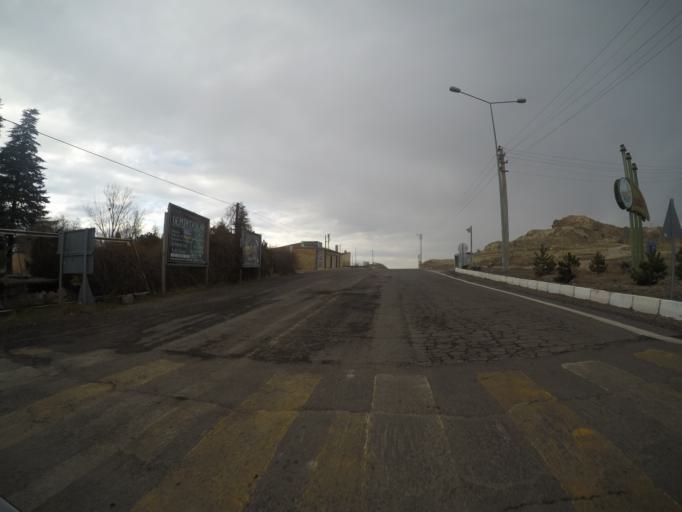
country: TR
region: Nevsehir
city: Goereme
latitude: 38.6319
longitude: 34.8572
